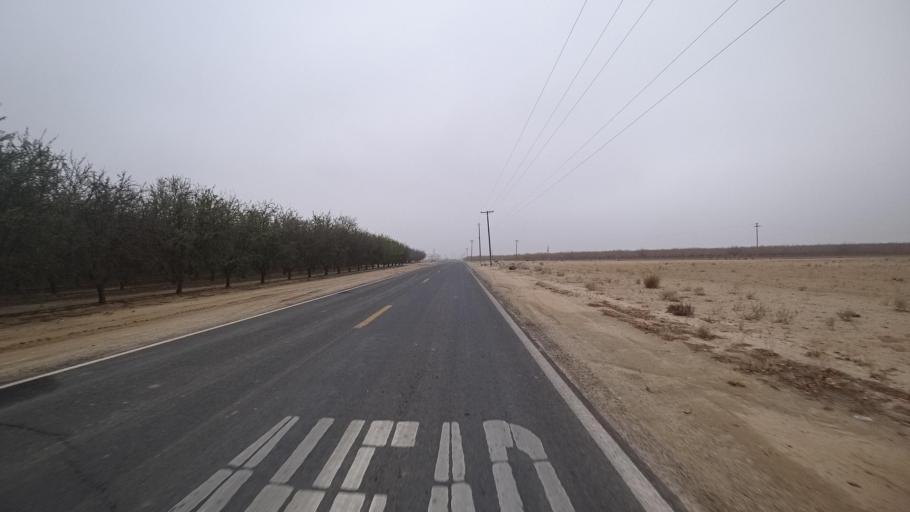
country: US
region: California
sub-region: Kern County
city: Lost Hills
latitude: 35.6094
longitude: -119.5803
